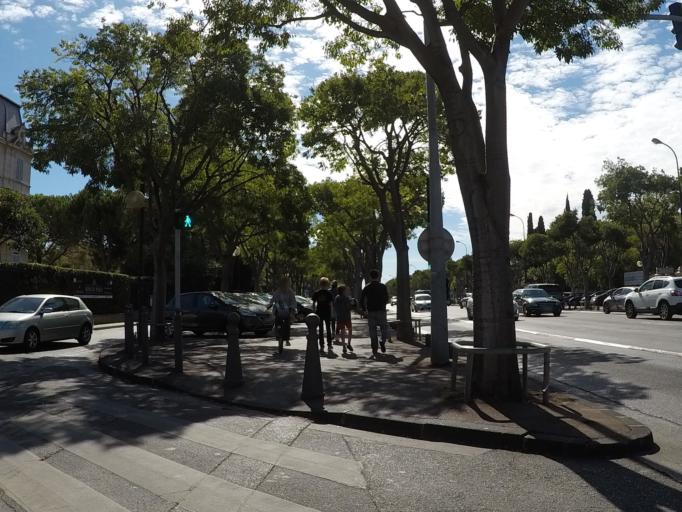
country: FR
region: Provence-Alpes-Cote d'Azur
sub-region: Departement des Bouches-du-Rhone
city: Marseille 08
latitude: 43.2674
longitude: 5.3835
